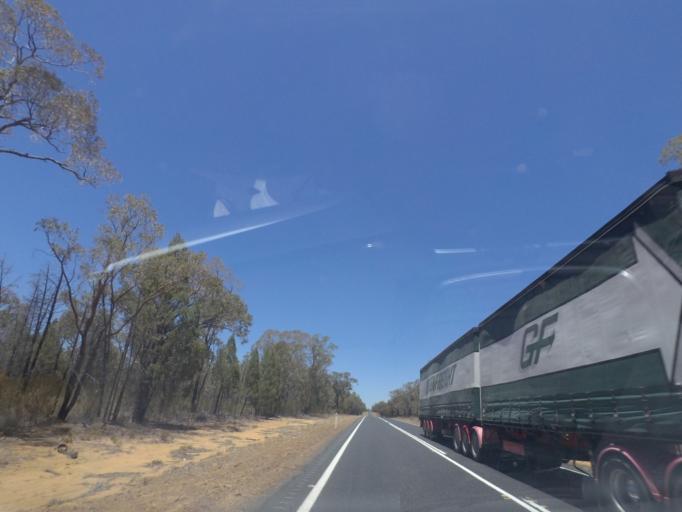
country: AU
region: New South Wales
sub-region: Narrabri
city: Narrabri
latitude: -30.7360
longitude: 149.5180
